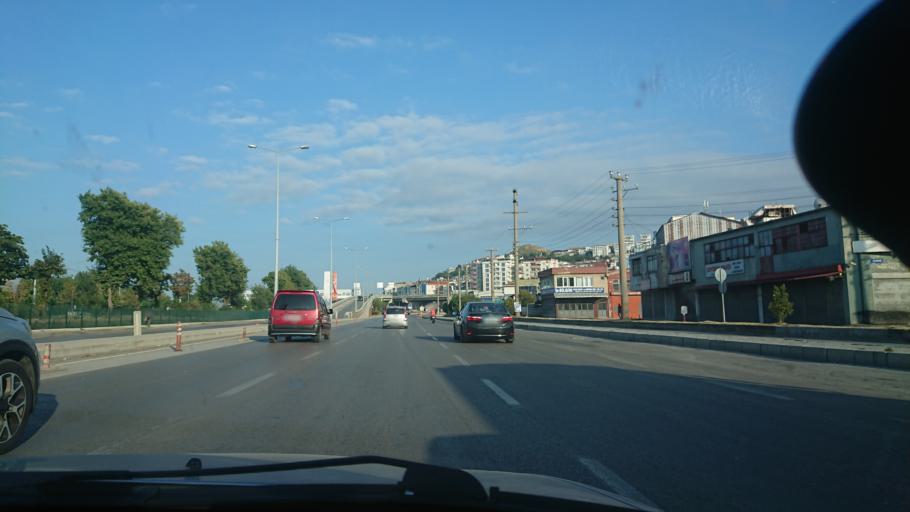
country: TR
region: Samsun
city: Samsun
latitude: 41.2739
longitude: 36.3623
